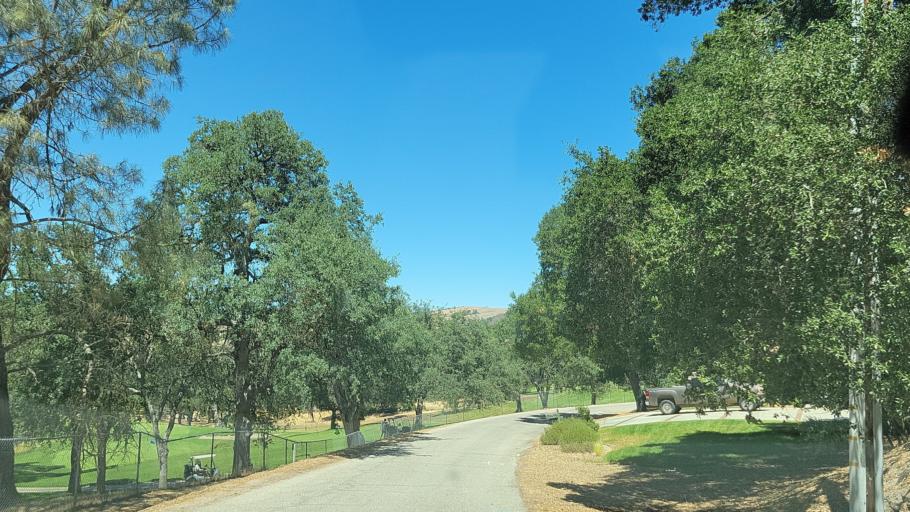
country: US
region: California
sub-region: San Luis Obispo County
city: Atascadero
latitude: 35.4688
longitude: -120.6470
